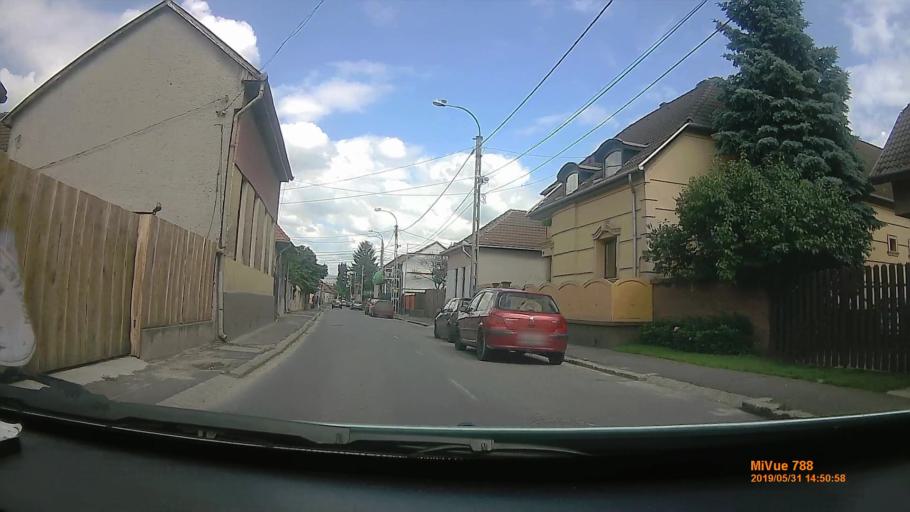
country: HU
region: Borsod-Abauj-Zemplen
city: Miskolc
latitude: 48.1011
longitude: 20.7681
